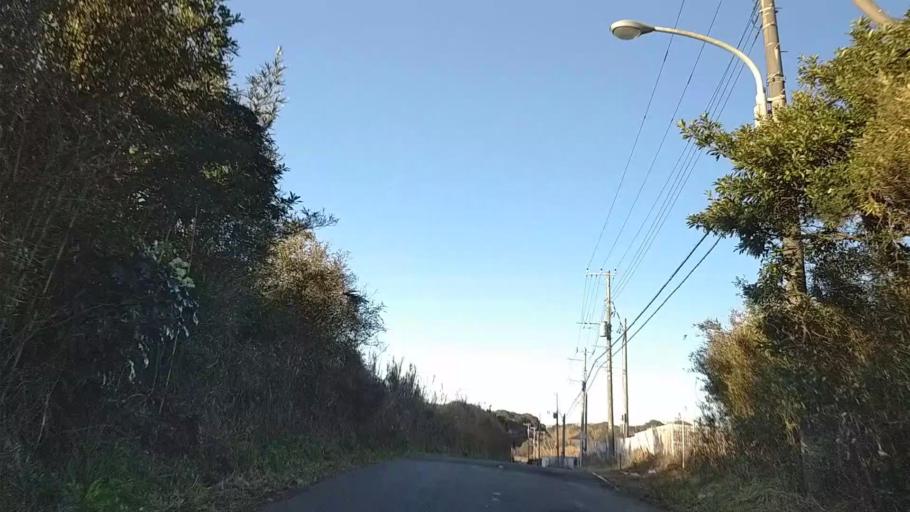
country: JP
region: Chiba
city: Asahi
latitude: 35.7080
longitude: 140.7284
